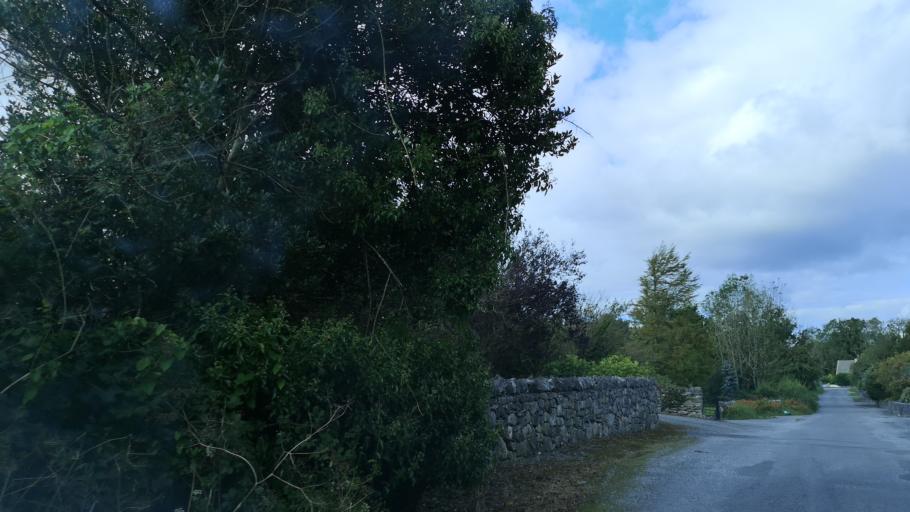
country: IE
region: Connaught
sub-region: County Galway
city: Moycullen
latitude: 53.3568
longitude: -9.1643
